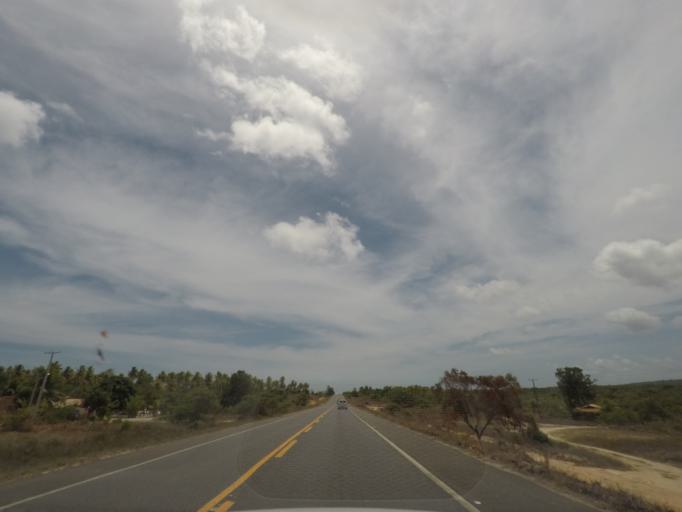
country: BR
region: Bahia
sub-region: Conde
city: Conde
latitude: -11.8529
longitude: -37.6338
